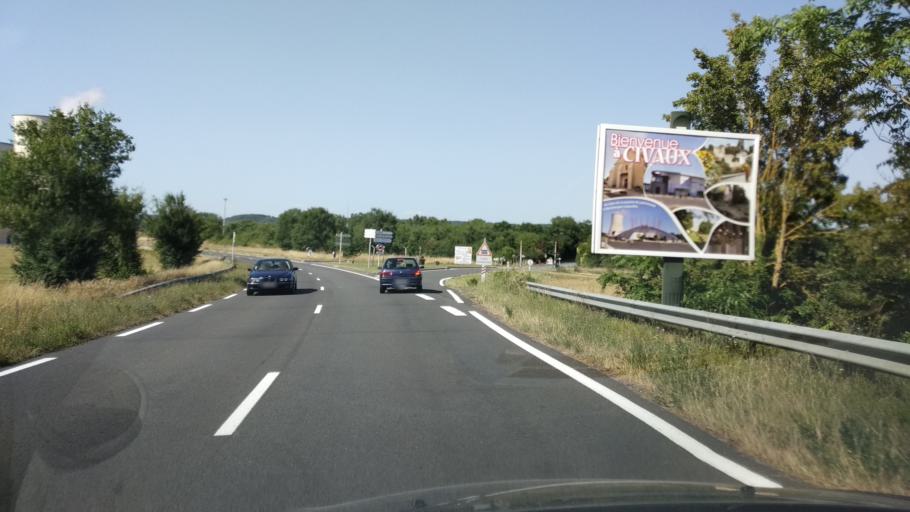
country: FR
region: Poitou-Charentes
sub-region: Departement de la Vienne
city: Lussac-les-Chateaux
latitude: 46.4413
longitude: 0.6566
